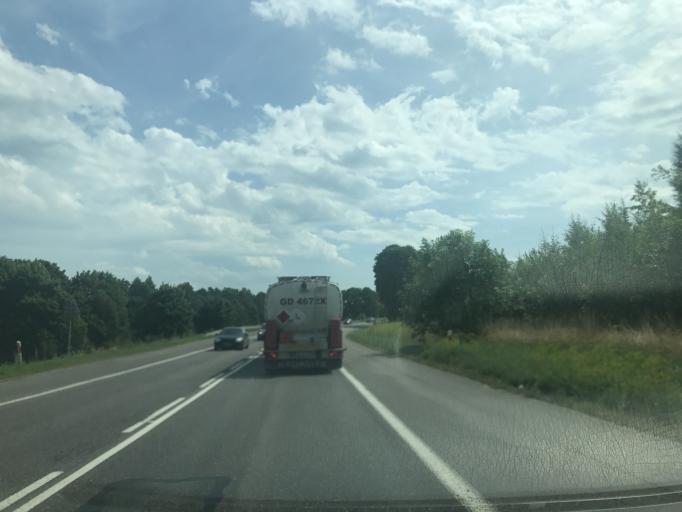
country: PL
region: Warmian-Masurian Voivodeship
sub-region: Powiat ostrodzki
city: Ostroda
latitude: 53.6696
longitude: 20.0366
